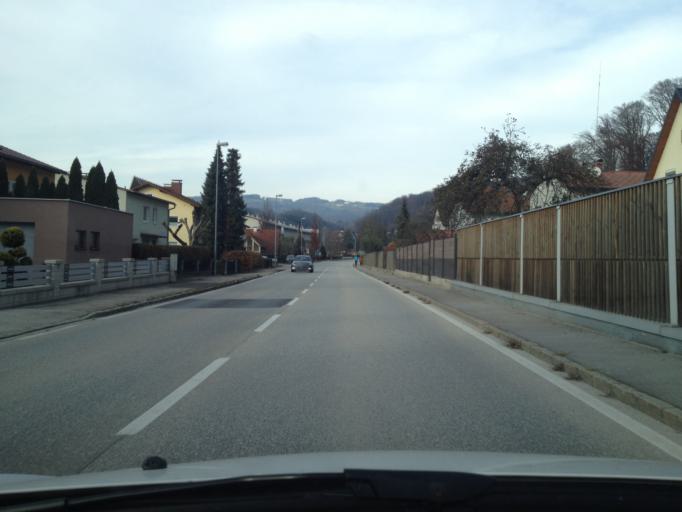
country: AT
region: Upper Austria
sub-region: Politischer Bezirk Urfahr-Umgebung
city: Steyregg
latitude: 48.3235
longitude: 14.3402
